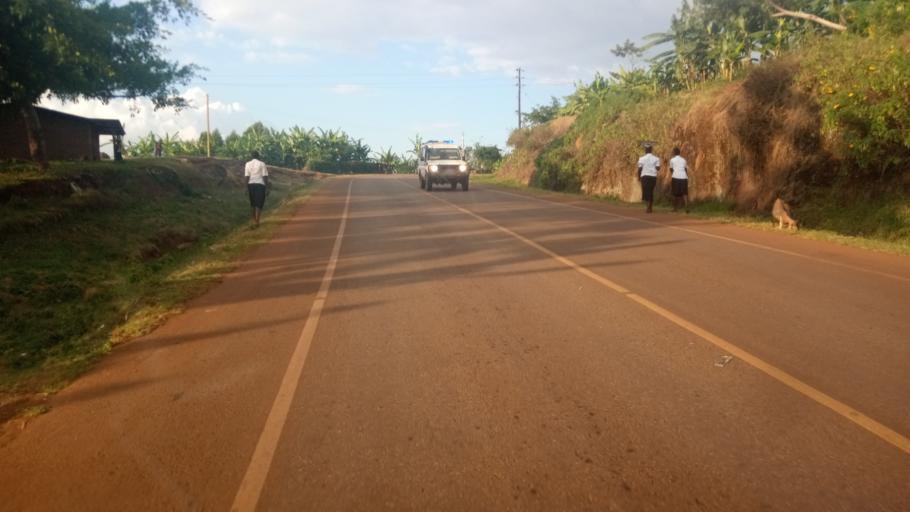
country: UG
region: Eastern Region
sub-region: Sironko District
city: Sironko
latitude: 1.3203
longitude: 34.3432
